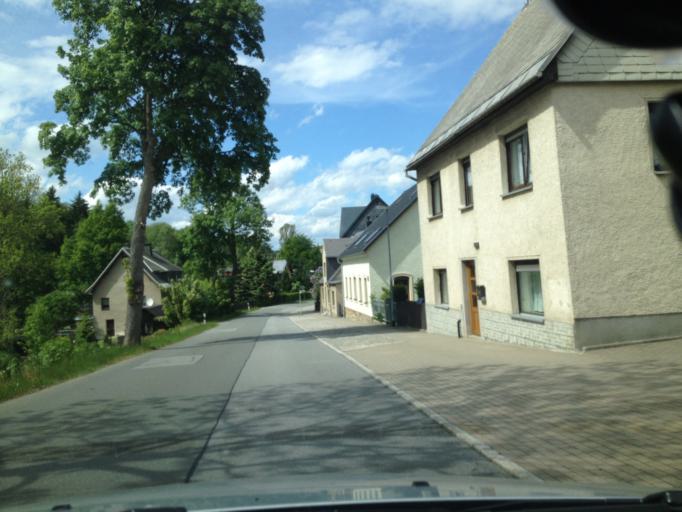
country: DE
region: Saxony
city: Barenstein
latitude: 50.5270
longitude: 12.9958
